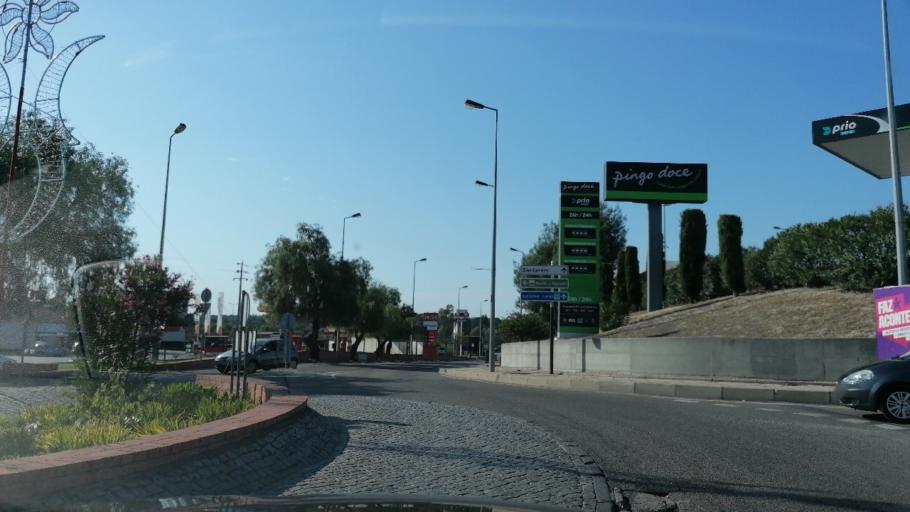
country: PT
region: Santarem
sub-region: Coruche
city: Coruche
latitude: 38.9647
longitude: -8.5335
